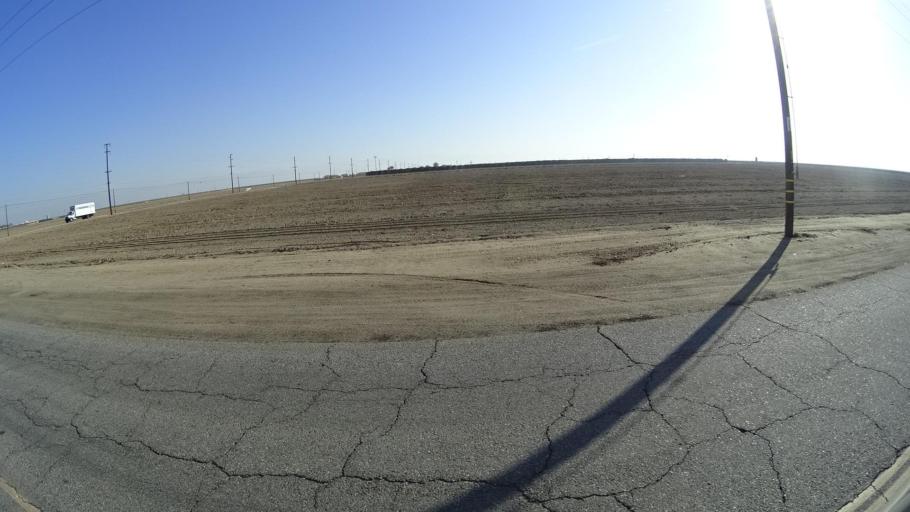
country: US
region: California
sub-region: Tulare County
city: Richgrove
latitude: 35.7753
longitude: -119.1697
